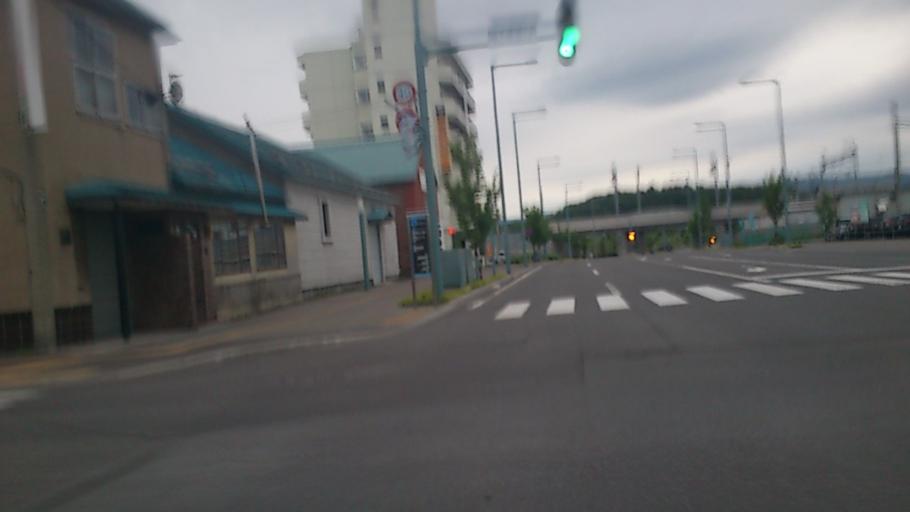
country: JP
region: Hokkaido
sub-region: Asahikawa-shi
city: Asahikawa
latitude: 43.7610
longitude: 142.3708
